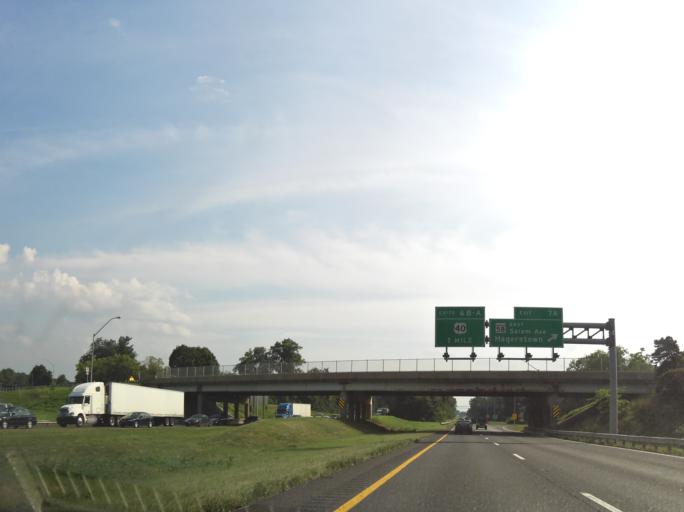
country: US
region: Maryland
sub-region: Washington County
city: Maugansville
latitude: 39.6642
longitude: -77.7396
